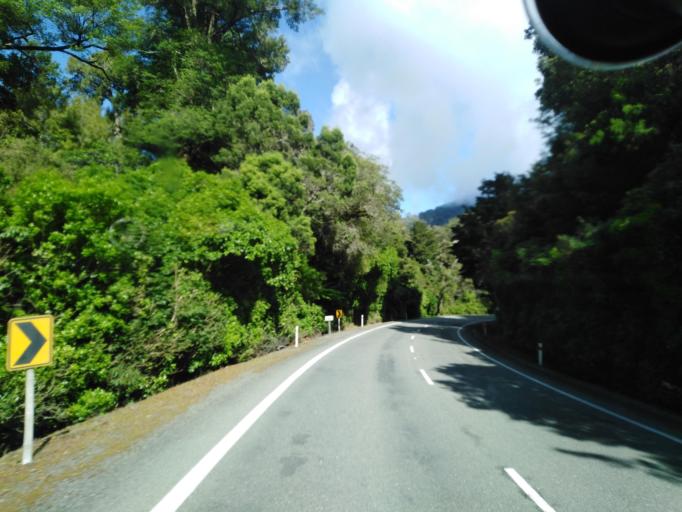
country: NZ
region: Nelson
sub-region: Nelson City
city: Nelson
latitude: -41.3015
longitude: 173.5748
